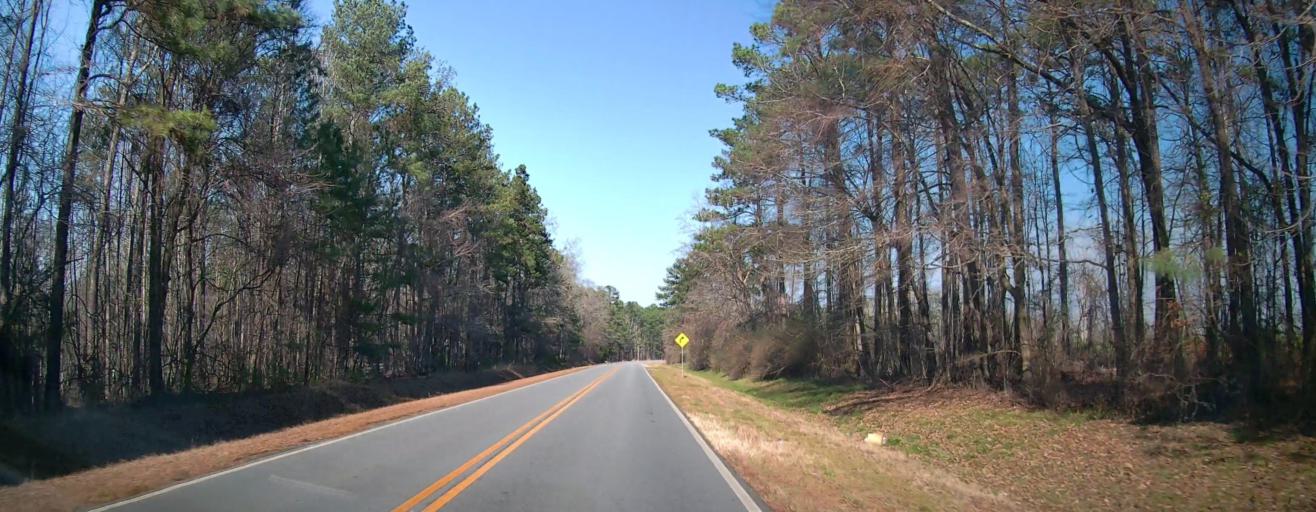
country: US
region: Georgia
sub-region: Monroe County
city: Forsyth
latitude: 33.0962
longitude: -83.8355
